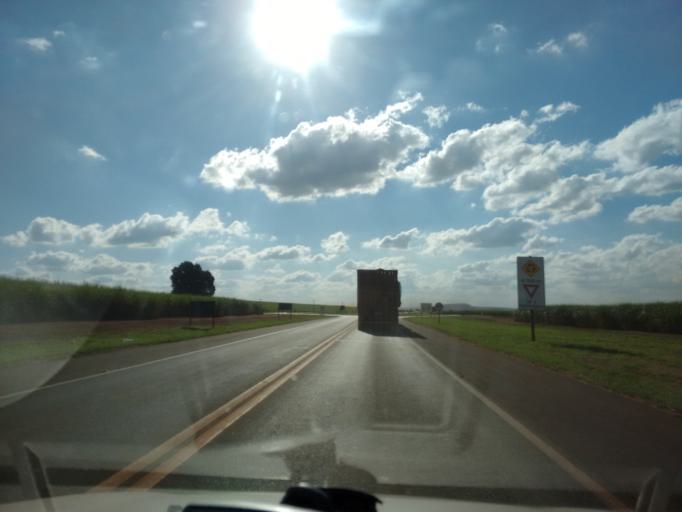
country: BR
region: Sao Paulo
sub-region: Americo Brasiliense
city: Americo Brasiliense
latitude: -21.6147
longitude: -48.0306
